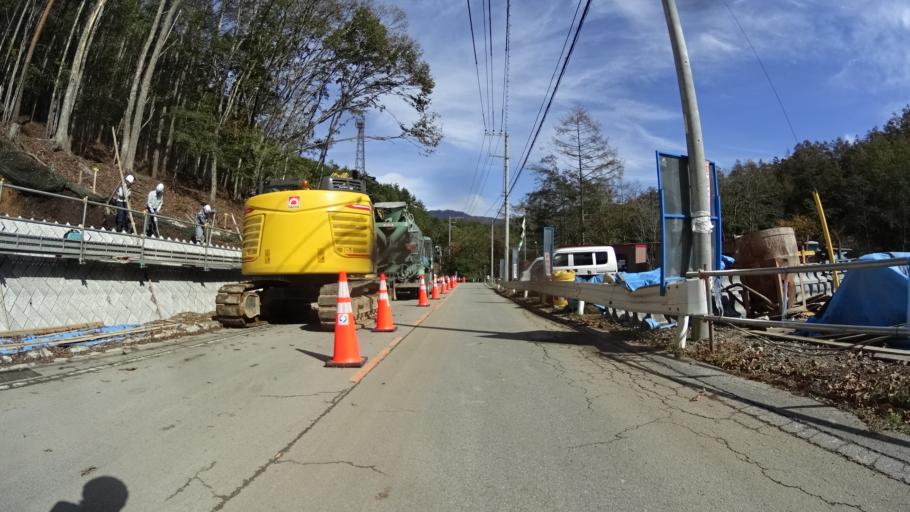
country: JP
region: Yamanashi
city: Enzan
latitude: 35.7955
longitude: 138.8092
